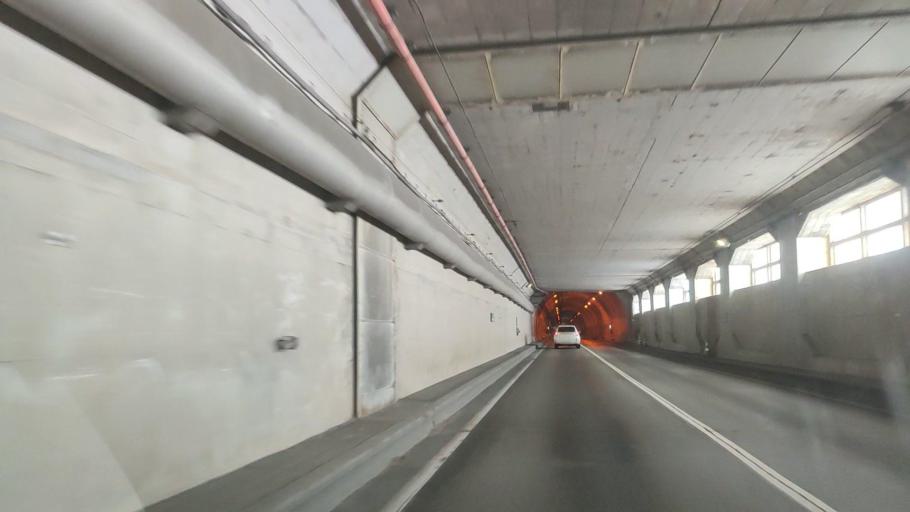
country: JP
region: Hokkaido
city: Rumoi
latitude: 43.7975
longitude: 141.3774
